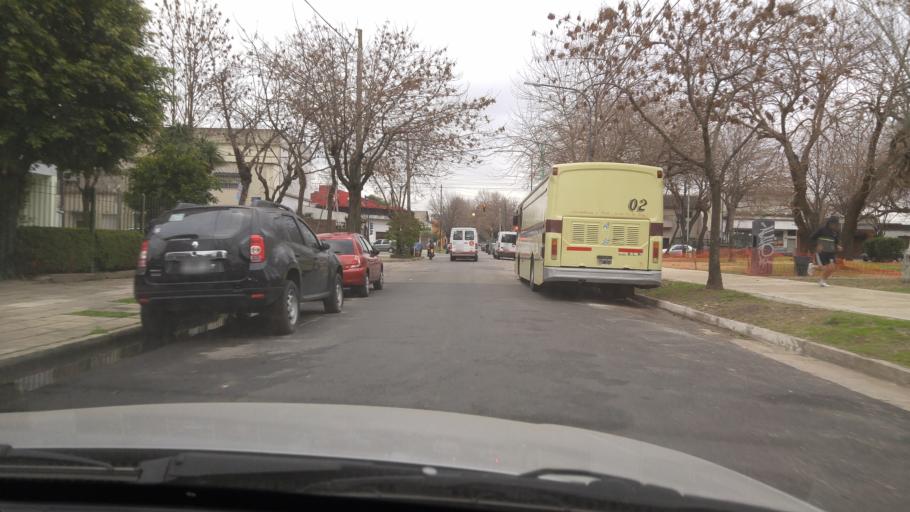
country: AR
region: Buenos Aires
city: Caseros
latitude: -34.6202
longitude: -58.5284
